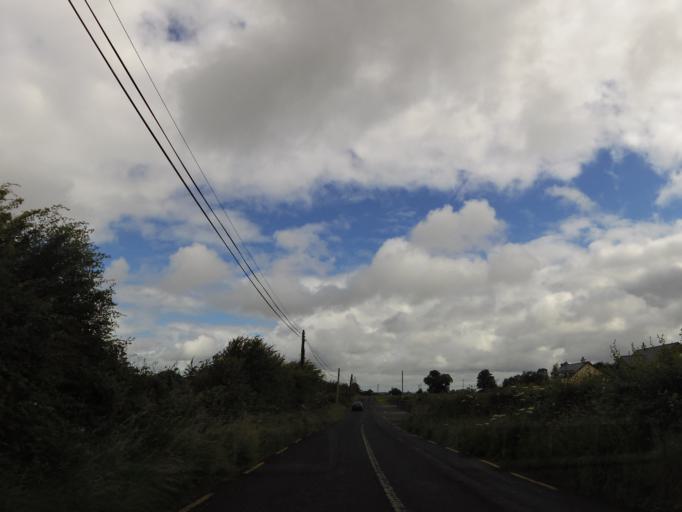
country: IE
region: Connaught
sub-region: County Galway
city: Loughrea
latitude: 53.4219
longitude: -8.5073
